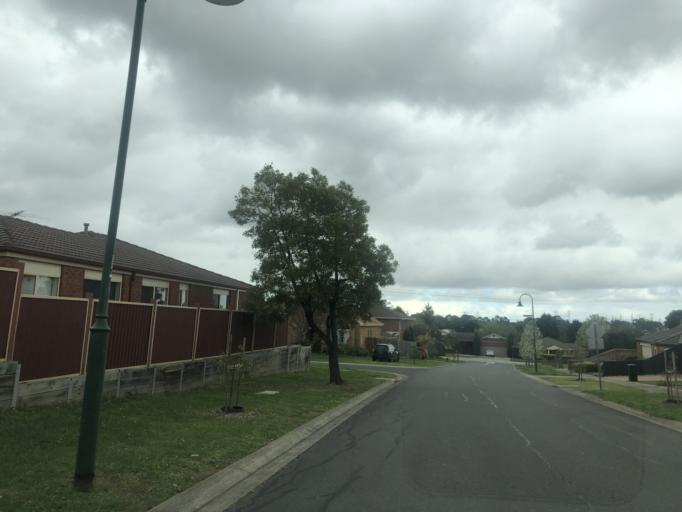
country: AU
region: Victoria
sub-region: Knox
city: Rowville
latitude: -37.9394
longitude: 145.2498
